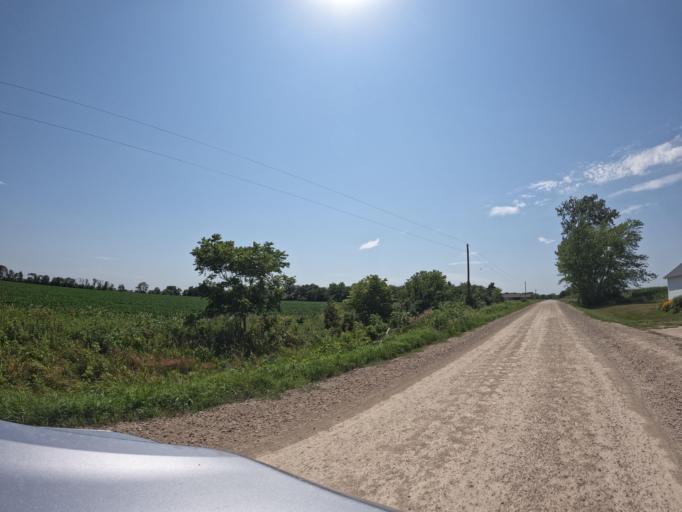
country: US
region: Iowa
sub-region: Henry County
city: Mount Pleasant
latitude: 40.8900
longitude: -91.6441
